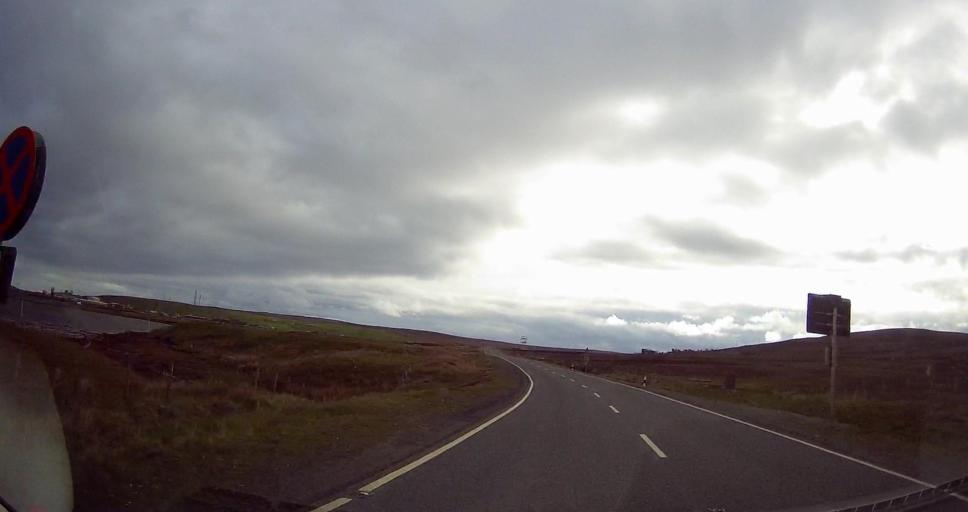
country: GB
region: Scotland
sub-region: Shetland Islands
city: Lerwick
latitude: 60.4361
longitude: -1.2836
